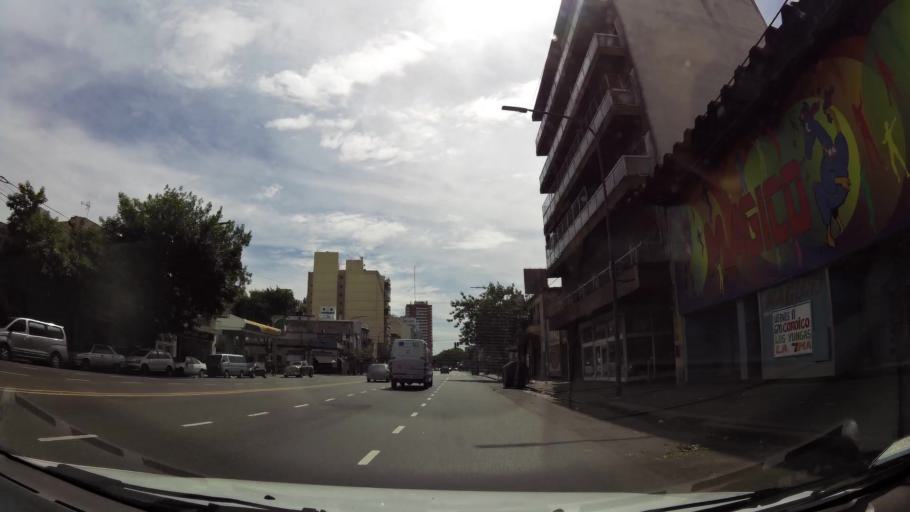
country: AR
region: Buenos Aires F.D.
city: Villa Santa Rita
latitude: -34.6390
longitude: -58.5180
